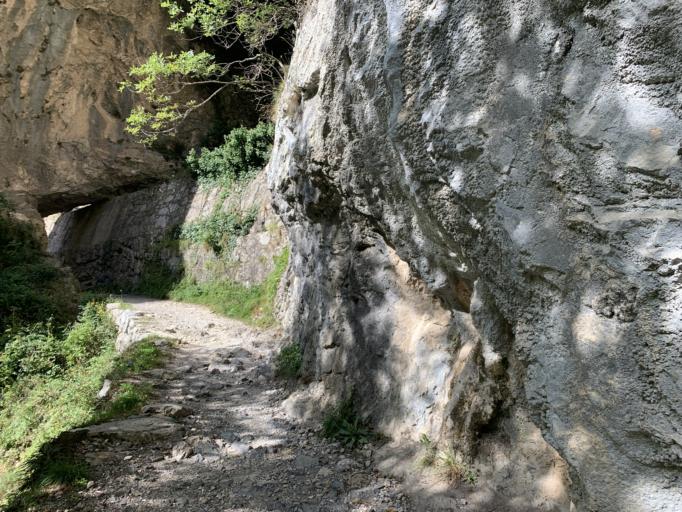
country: ES
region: Castille and Leon
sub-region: Provincia de Leon
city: Posada de Valdeon
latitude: 43.2311
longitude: -4.8937
